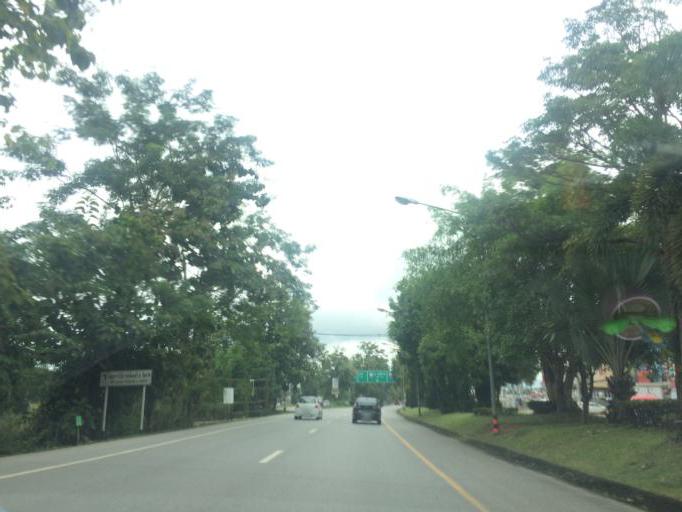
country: TH
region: Chiang Rai
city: Chiang Rai
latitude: 19.8721
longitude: 99.8268
